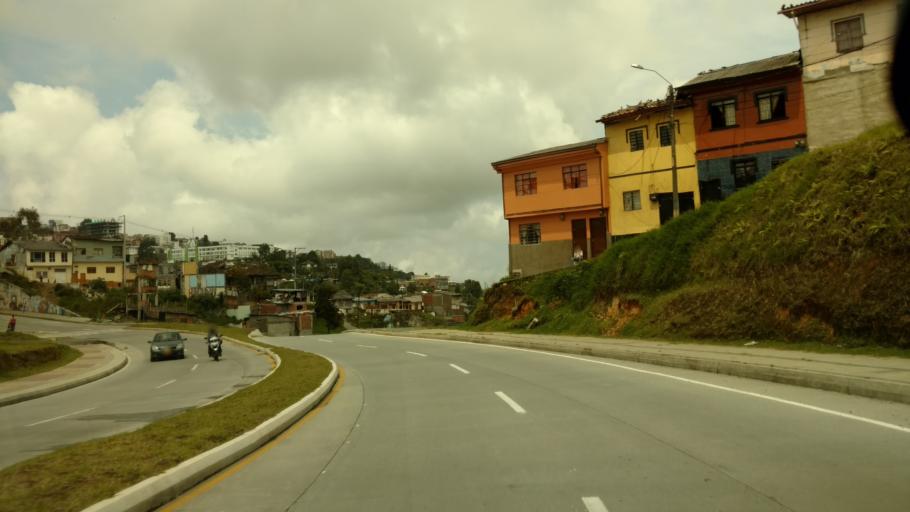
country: CO
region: Caldas
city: Manizales
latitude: 5.0735
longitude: -75.5134
